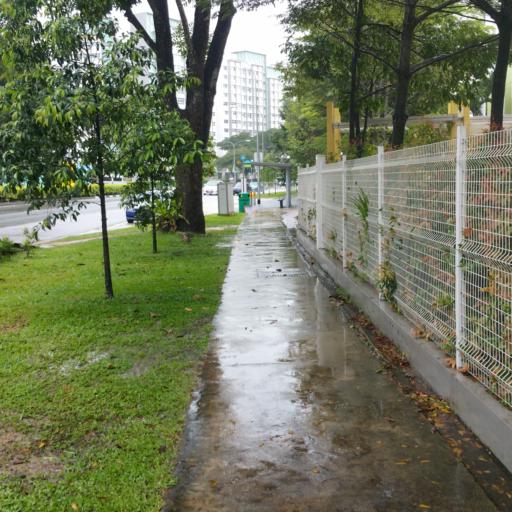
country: MY
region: Johor
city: Kampung Pasir Gudang Baru
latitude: 1.4172
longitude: 103.8461
